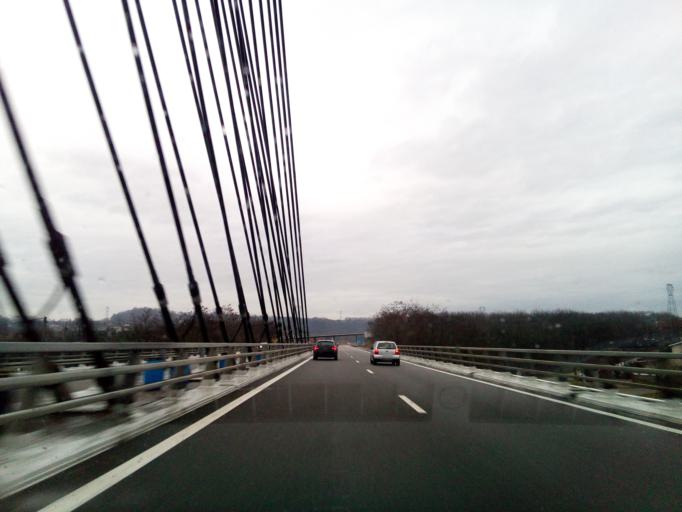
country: FR
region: Rhone-Alpes
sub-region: Departement de l'Isere
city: Saint-Lattier
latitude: 45.0832
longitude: 5.2153
